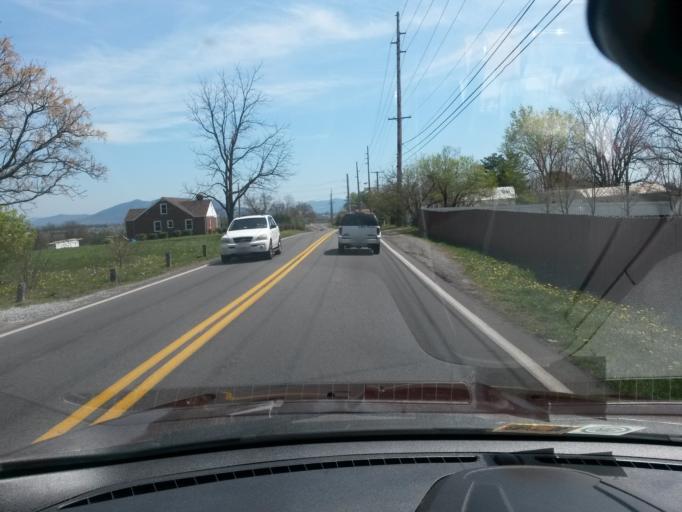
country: US
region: Virginia
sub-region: City of Roanoke
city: Roanoke
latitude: 37.3026
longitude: -79.9888
